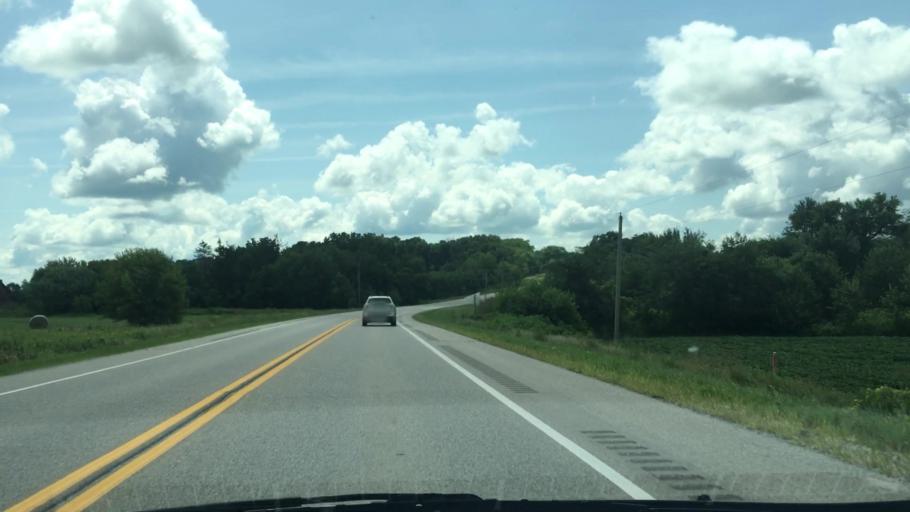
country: US
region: Iowa
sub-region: Johnson County
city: Solon
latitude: 41.7519
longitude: -91.4746
